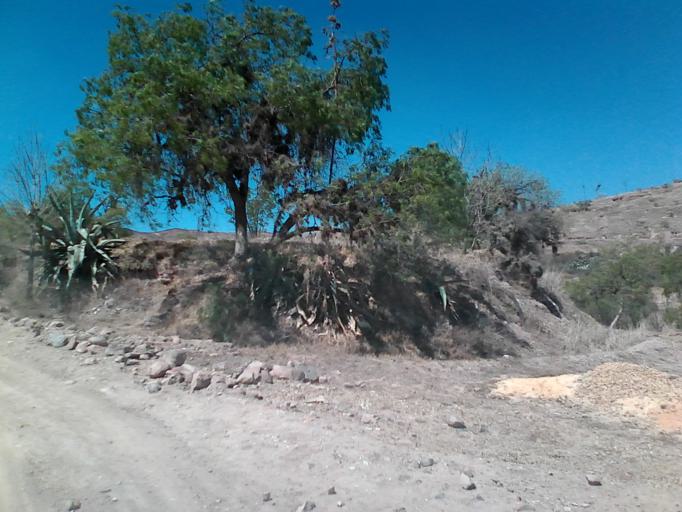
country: CO
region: Boyaca
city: Sachica
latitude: 5.5676
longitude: -73.5376
